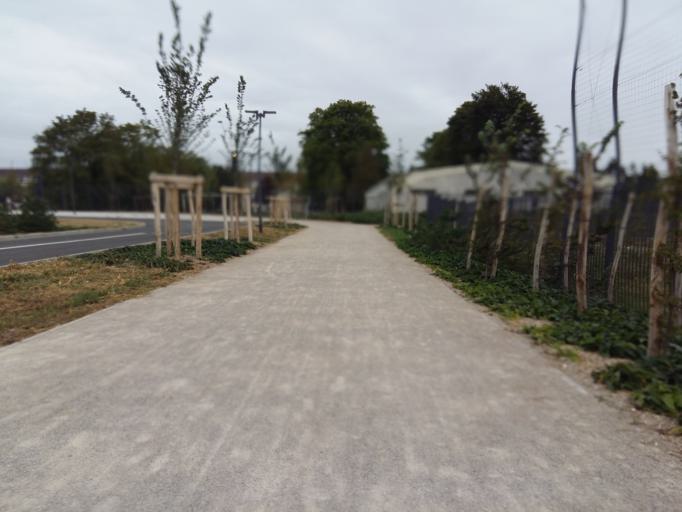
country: FR
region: Picardie
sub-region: Departement de la Somme
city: Amiens
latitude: 49.8757
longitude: 2.3009
